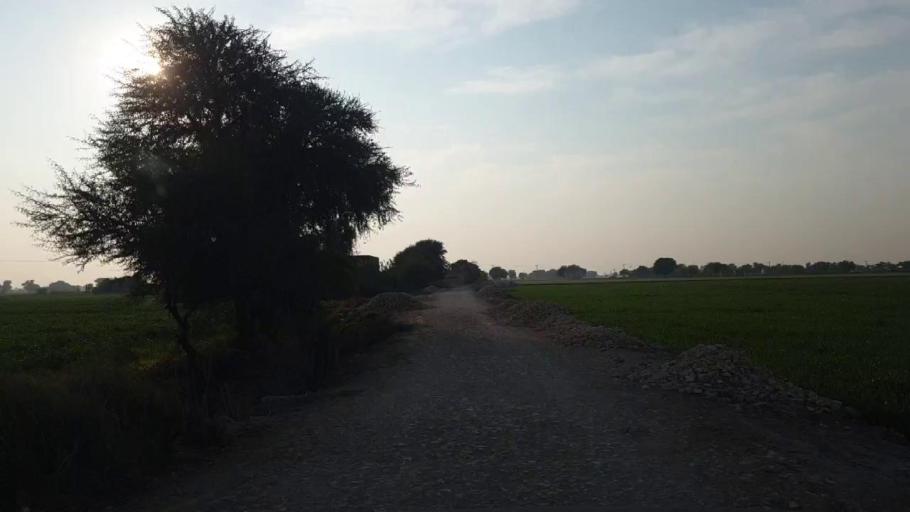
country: PK
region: Sindh
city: Shahpur Chakar
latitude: 26.1528
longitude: 68.6237
